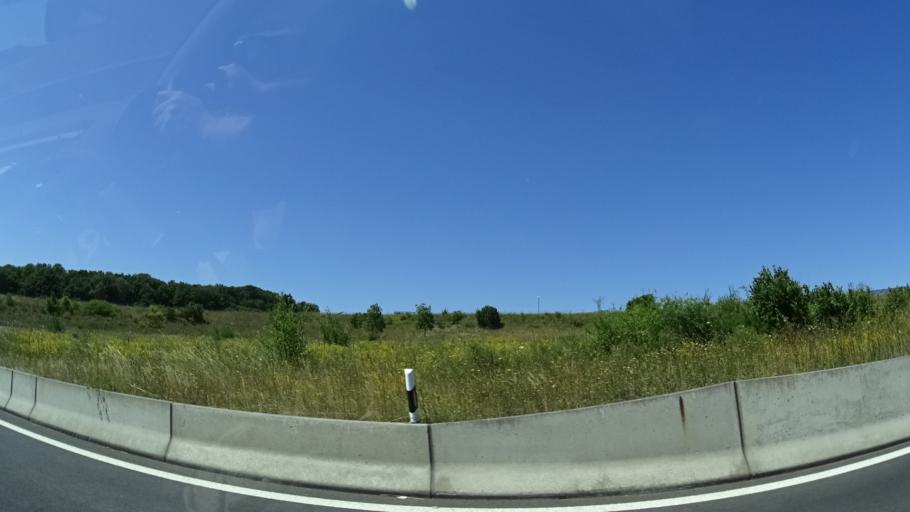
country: DE
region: Bavaria
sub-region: Regierungsbezirk Unterfranken
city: Rannungen
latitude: 50.2002
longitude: 10.2165
